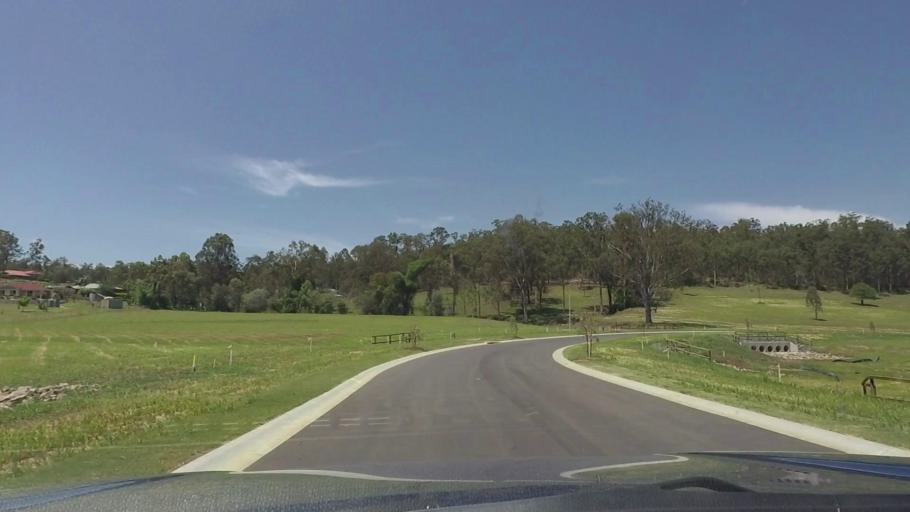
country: AU
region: Queensland
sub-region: Logan
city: Cedar Vale
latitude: -27.8893
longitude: 152.9914
